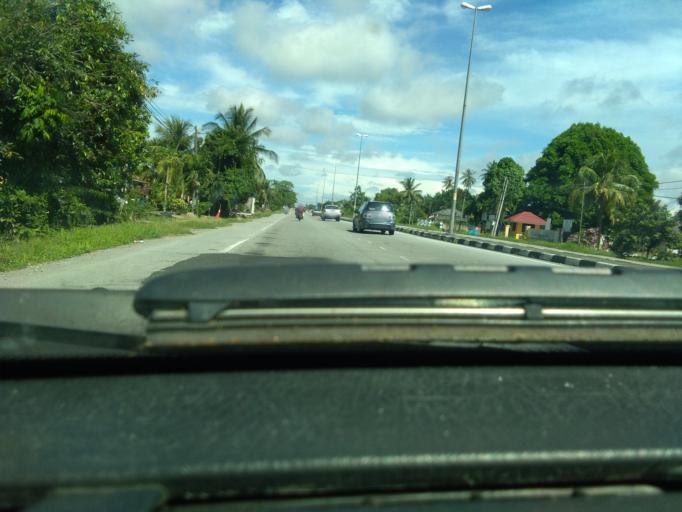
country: MY
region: Perak
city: Bagan Serai
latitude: 5.0016
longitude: 100.5512
